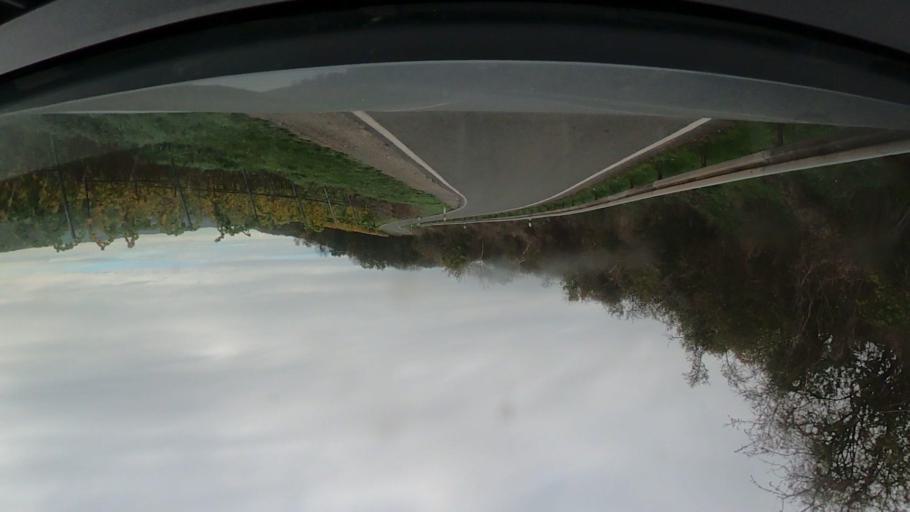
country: DE
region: Thuringia
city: Bad Sulza
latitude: 51.1031
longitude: 11.6406
